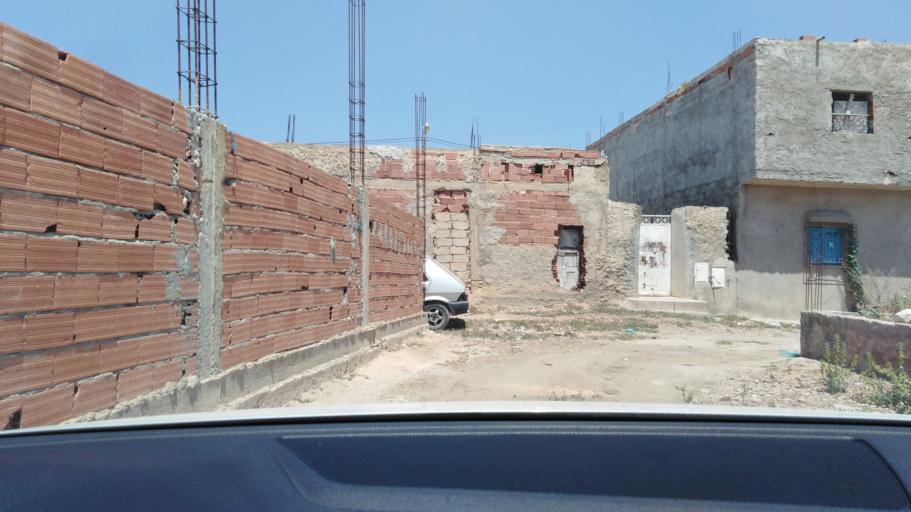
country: TN
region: Al Qayrawan
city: Sbikha
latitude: 36.1166
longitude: 10.0989
